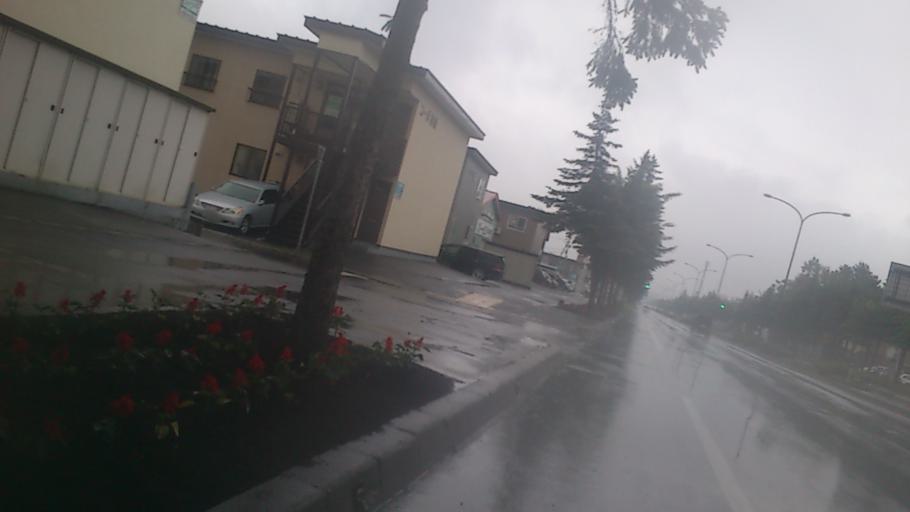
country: JP
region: Hokkaido
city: Obihiro
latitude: 42.9076
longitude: 143.1317
